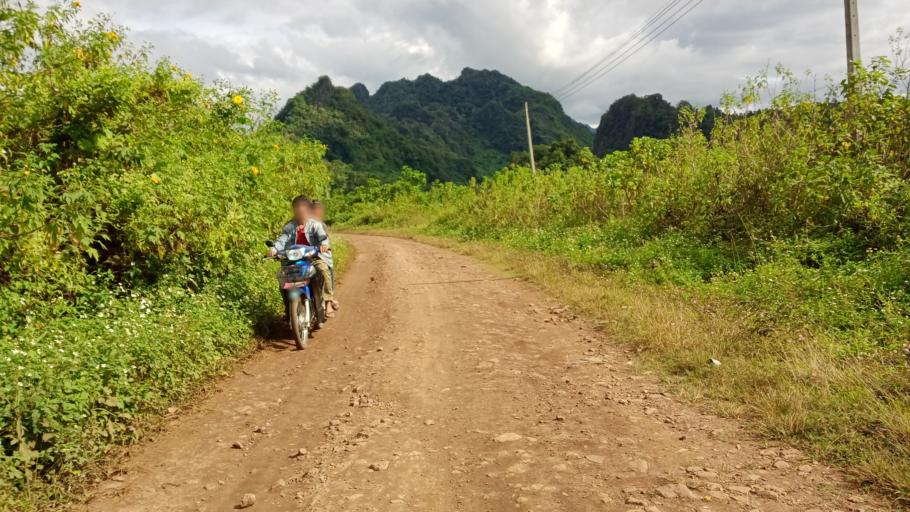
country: LA
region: Xiangkhoang
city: Phonsavan
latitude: 19.1047
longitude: 102.9312
